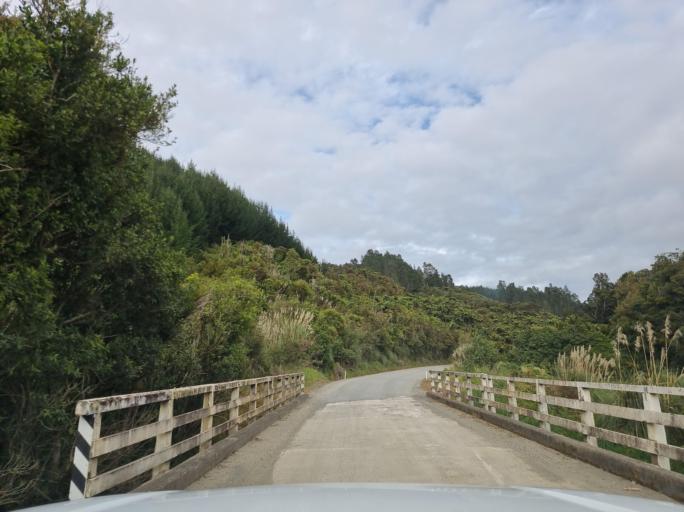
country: NZ
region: Northland
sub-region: Whangarei
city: Ruakaka
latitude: -36.0525
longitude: 174.4035
